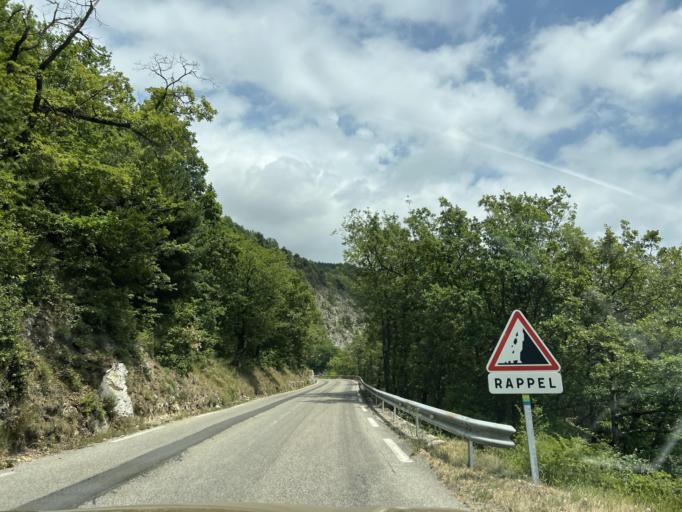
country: FR
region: Provence-Alpes-Cote d'Azur
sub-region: Departement des Alpes-Maritimes
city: Tourrettes-sur-Loup
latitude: 43.7960
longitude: 6.9528
